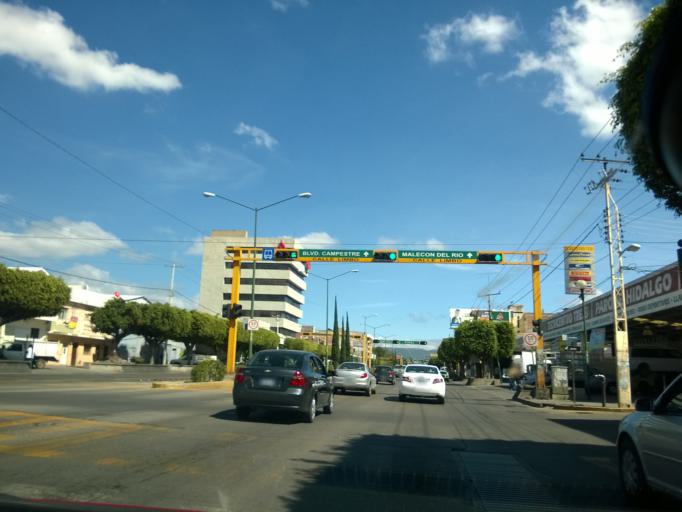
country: MX
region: Guanajuato
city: Leon
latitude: 21.1336
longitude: -101.6875
